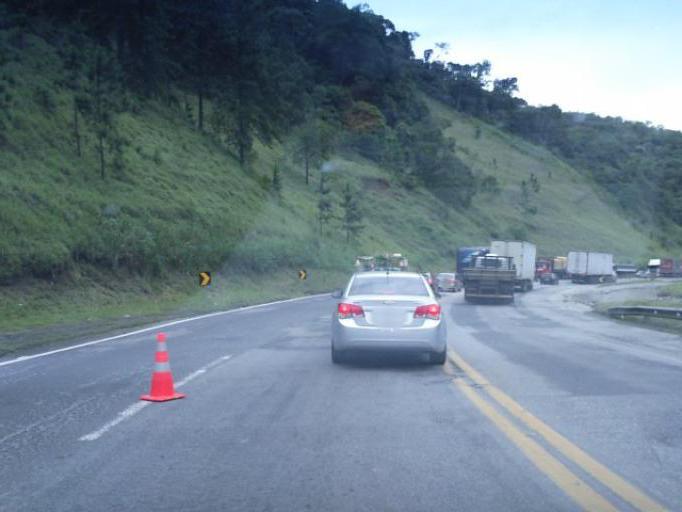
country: BR
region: Sao Paulo
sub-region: Juquitiba
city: Juquitiba
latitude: -24.0562
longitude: -47.2153
